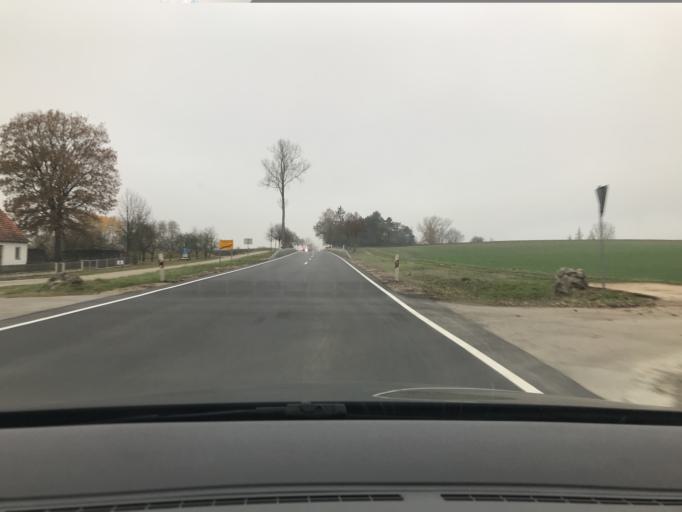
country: DE
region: Bavaria
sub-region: Regierungsbezirk Mittelfranken
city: Monchsroth
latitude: 49.0468
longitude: 10.3541
